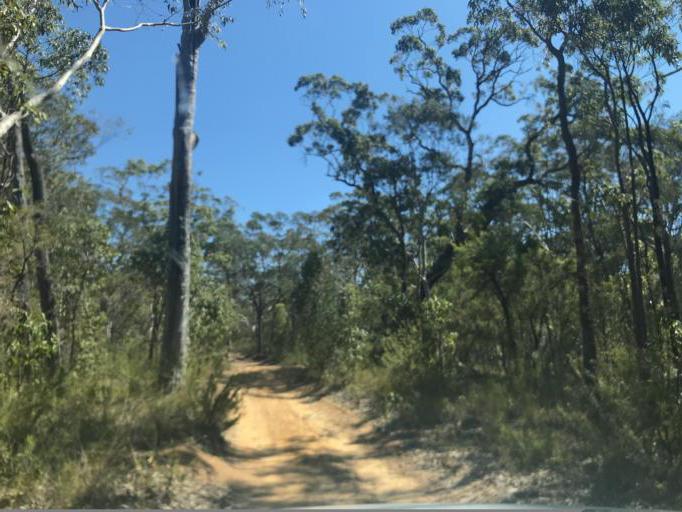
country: AU
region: New South Wales
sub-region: Wyong Shire
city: Little Jilliby
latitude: -33.1470
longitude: 151.0994
